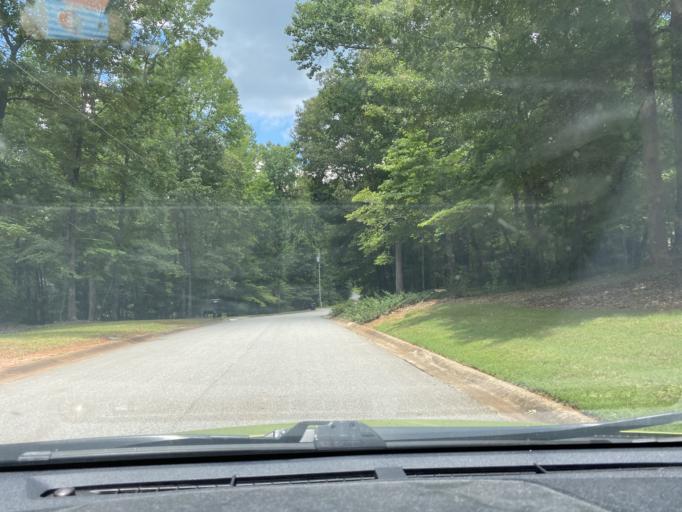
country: US
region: Georgia
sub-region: Fulton County
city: Palmetto
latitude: 33.4386
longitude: -84.6807
